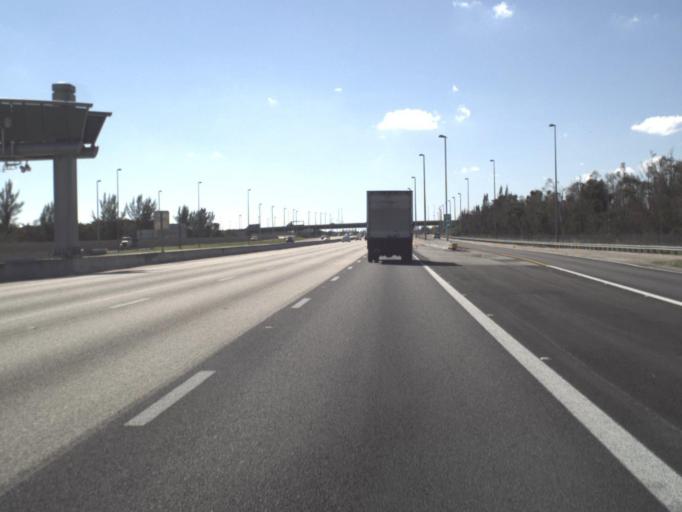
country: US
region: Florida
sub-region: Miami-Dade County
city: Doral
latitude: 25.8462
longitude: -80.3875
